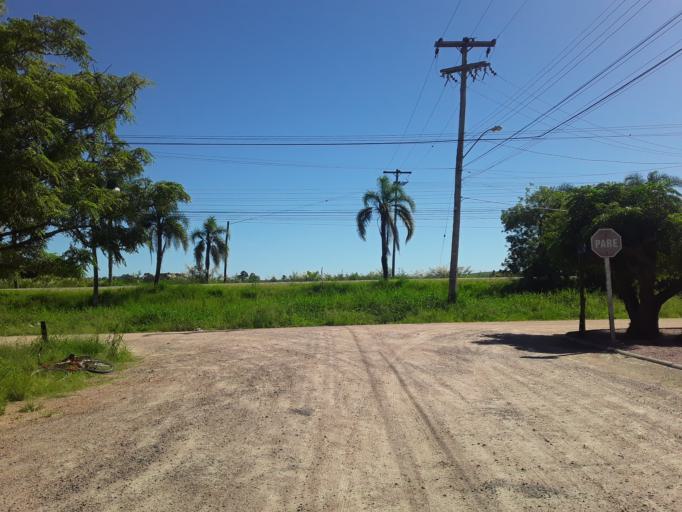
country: BR
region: Rio Grande do Sul
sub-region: Sao Lourenco Do Sul
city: Sao Lourenco do Sul
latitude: -31.3470
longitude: -51.9934
